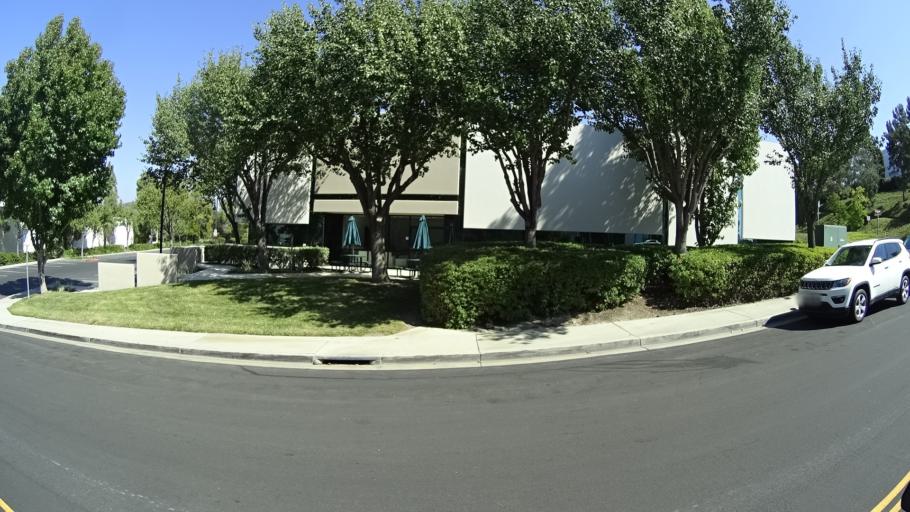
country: US
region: California
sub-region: Orange County
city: San Clemente
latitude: 33.4531
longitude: -117.6010
